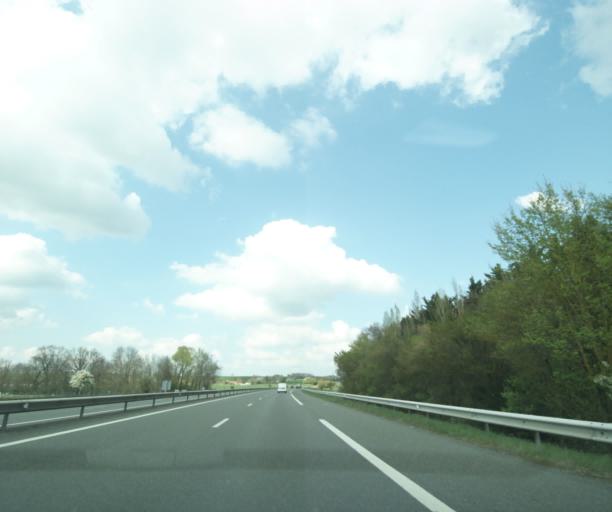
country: FR
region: Auvergne
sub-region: Departement de l'Allier
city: Bellenaves
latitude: 46.2105
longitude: 3.0973
